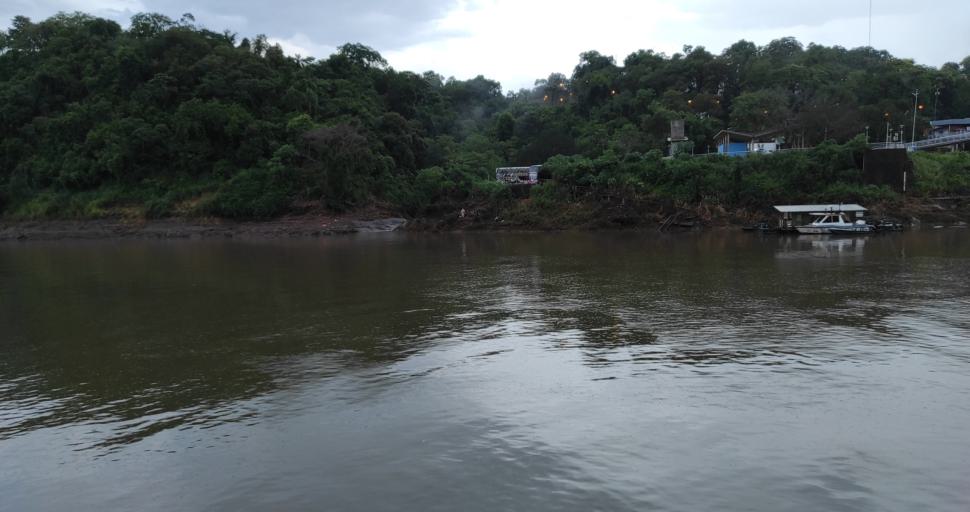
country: AR
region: Misiones
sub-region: Departamento de Iguazu
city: Puerto Iguazu
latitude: -25.5919
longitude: -54.5792
